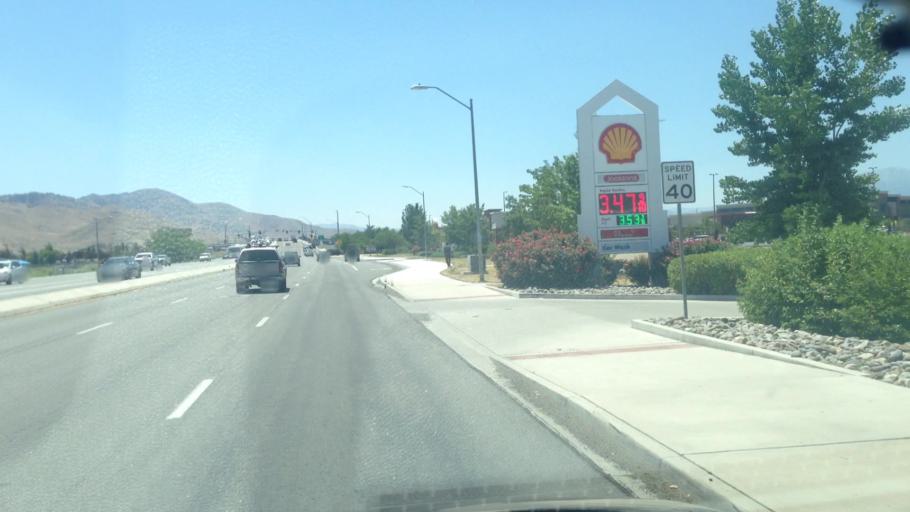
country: US
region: Nevada
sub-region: Washoe County
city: Sparks
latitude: 39.5333
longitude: -119.7137
